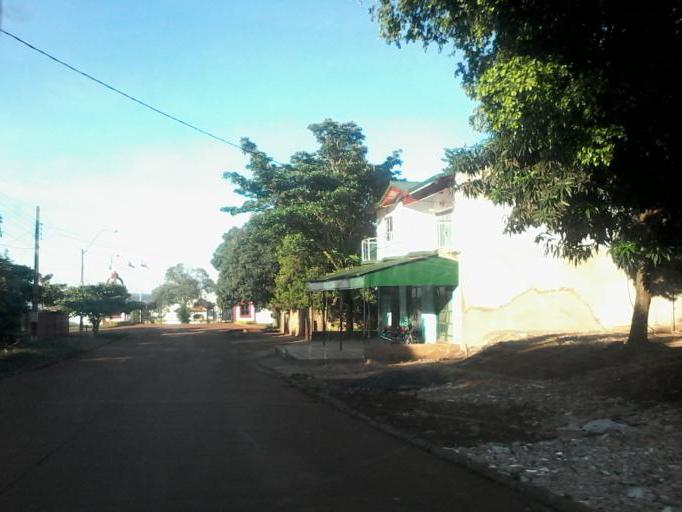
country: PY
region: Alto Parana
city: Ciudad del Este
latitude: -25.4376
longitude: -54.6432
